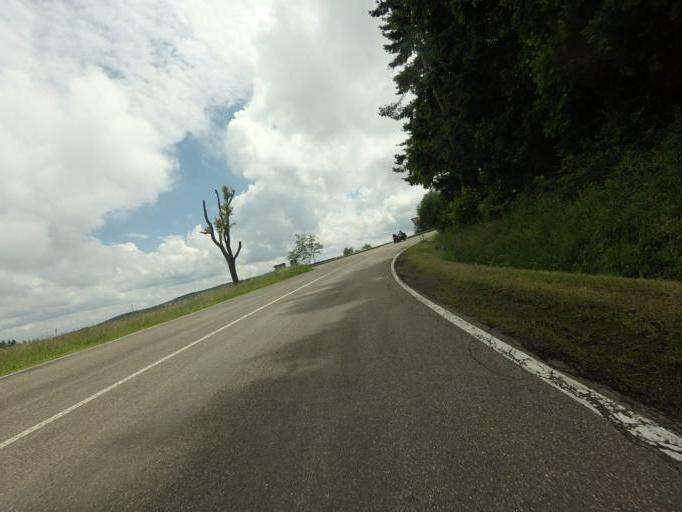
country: DE
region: Rheinland-Pfalz
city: Siebenbach
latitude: 50.3844
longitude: 7.0245
